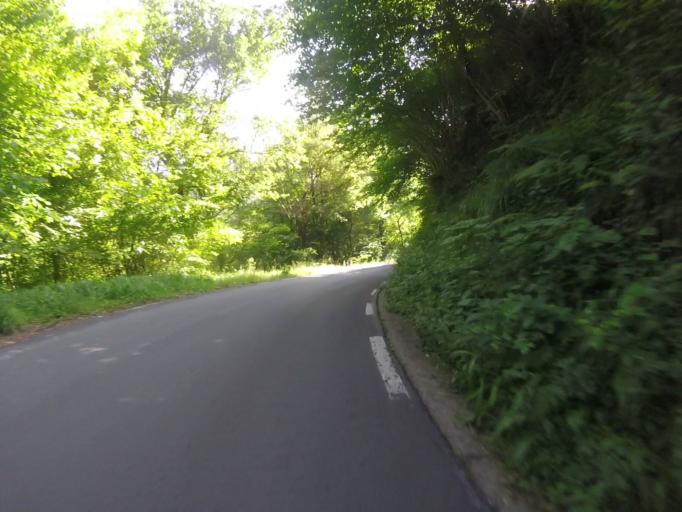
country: ES
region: Basque Country
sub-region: Provincia de Guipuzcoa
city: Beasain
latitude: 43.0756
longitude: -2.2255
